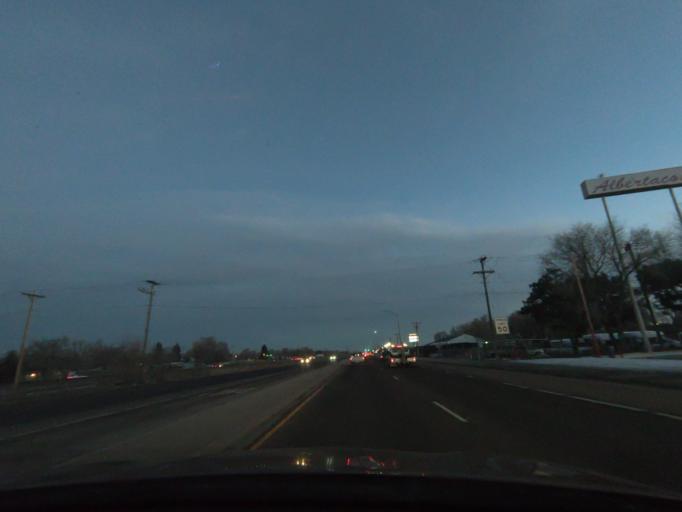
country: US
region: Colorado
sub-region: El Paso County
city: Security-Widefield
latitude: 38.7495
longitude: -104.7427
